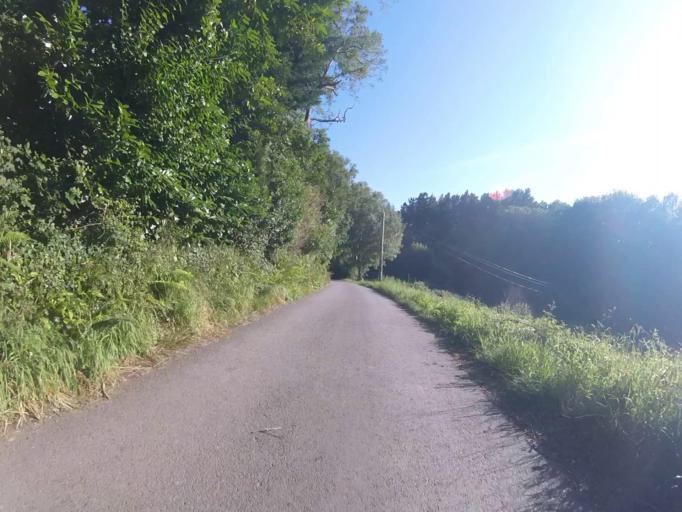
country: ES
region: Basque Country
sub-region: Provincia de Guipuzcoa
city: Fuenterrabia
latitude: 43.3734
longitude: -1.8113
